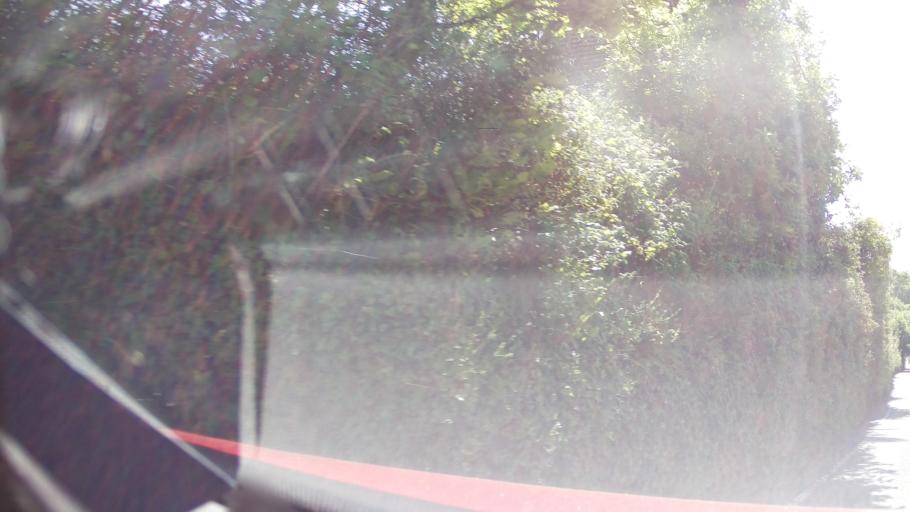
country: GB
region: England
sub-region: Devon
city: Newton Poppleford
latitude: 50.6829
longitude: -3.3056
